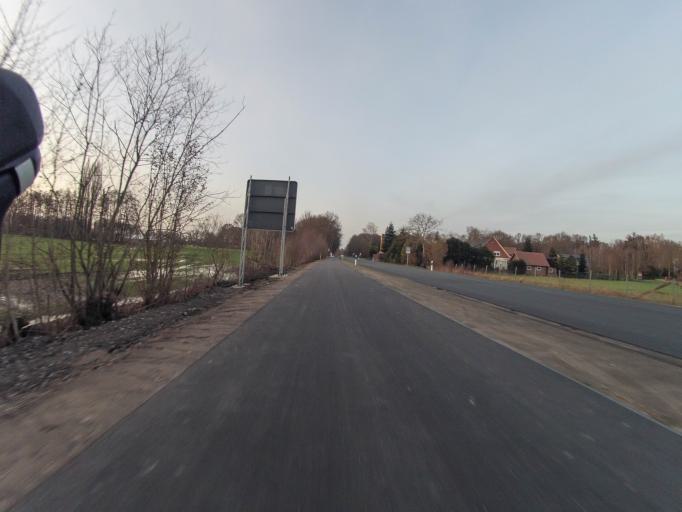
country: DE
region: North Rhine-Westphalia
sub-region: Regierungsbezirk Munster
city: Wettringen
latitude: 52.1999
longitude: 7.3235
